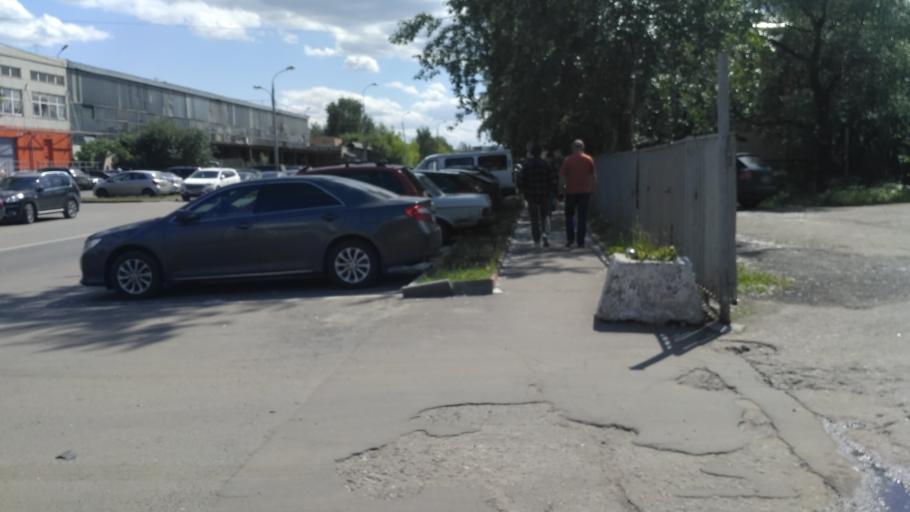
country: RU
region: Moscow
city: Kozeyevo
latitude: 55.8885
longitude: 37.6353
